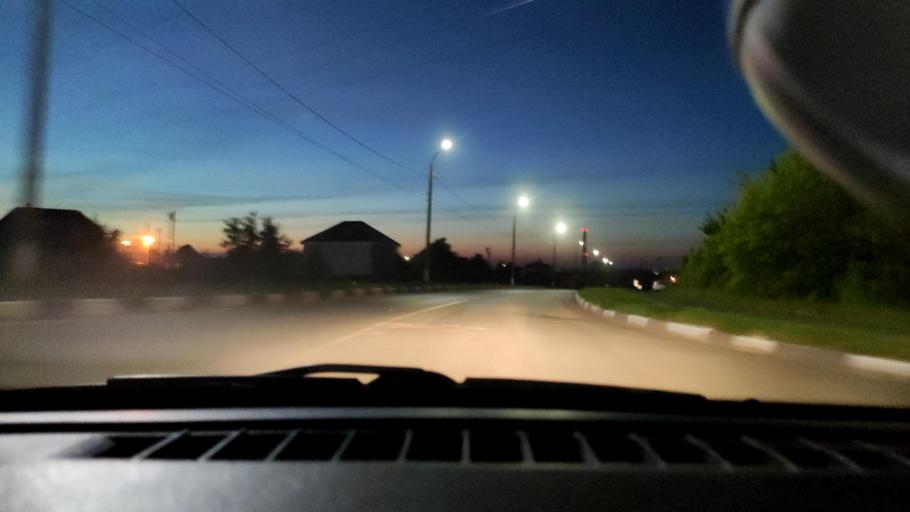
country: RU
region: Samara
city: Novokuybyshevsk
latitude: 53.0896
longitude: 49.9967
